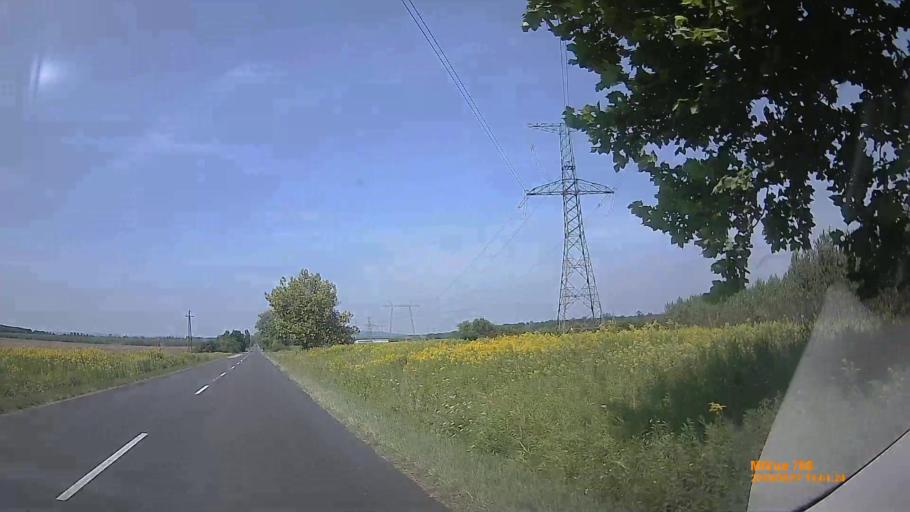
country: HU
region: Veszprem
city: Devecser
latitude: 47.0203
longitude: 17.4941
